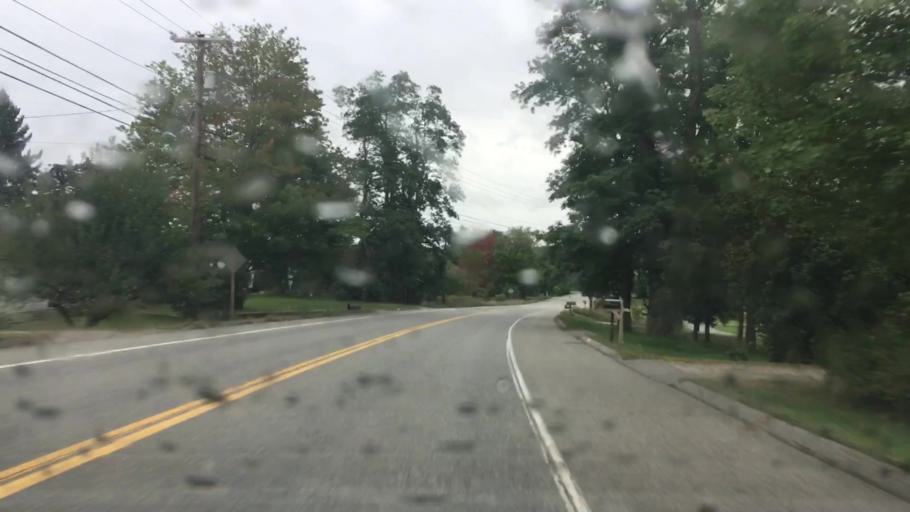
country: US
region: Maine
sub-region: Penobscot County
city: Orrington
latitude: 44.7220
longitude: -68.8261
